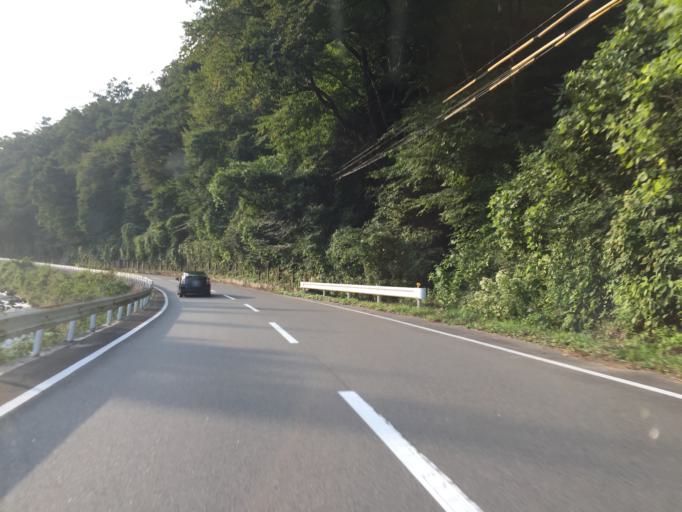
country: JP
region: Fukushima
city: Namie
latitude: 37.5533
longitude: 140.8383
